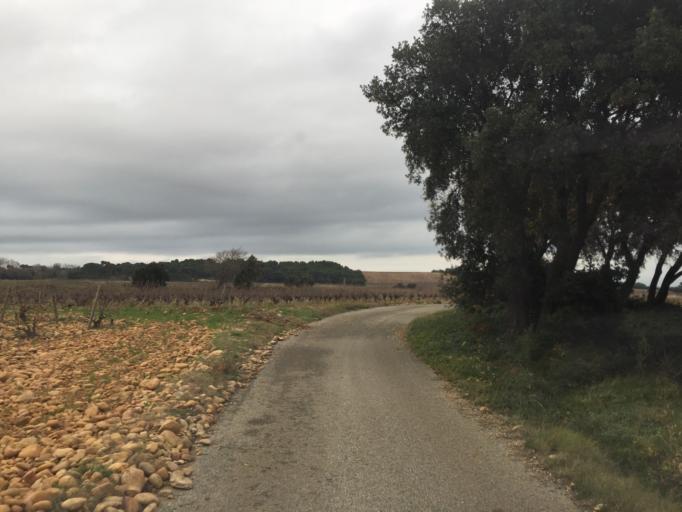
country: FR
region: Provence-Alpes-Cote d'Azur
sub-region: Departement du Vaucluse
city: Chateauneuf-du-Pape
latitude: 44.0433
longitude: 4.8519
